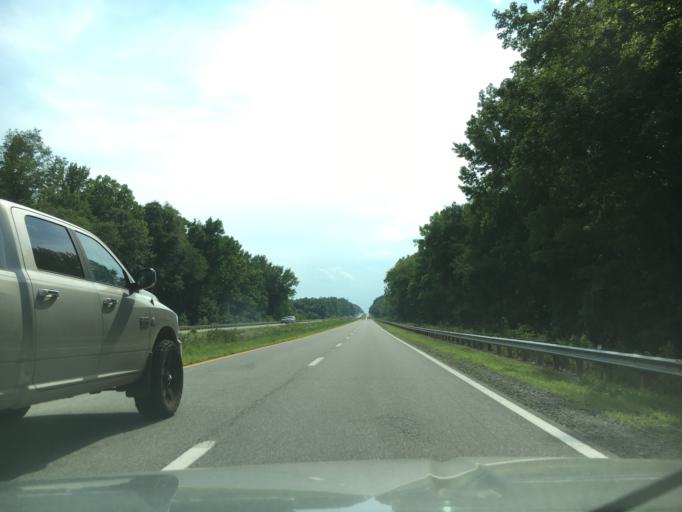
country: US
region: Virginia
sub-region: Mecklenburg County
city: Chase City
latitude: 36.8291
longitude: -78.6819
